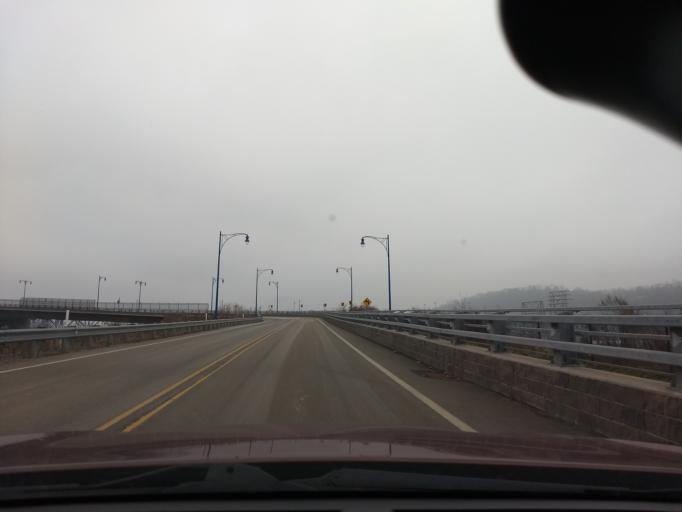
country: US
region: Pennsylvania
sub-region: Allegheny County
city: Rankin
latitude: 40.4100
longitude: -79.8813
